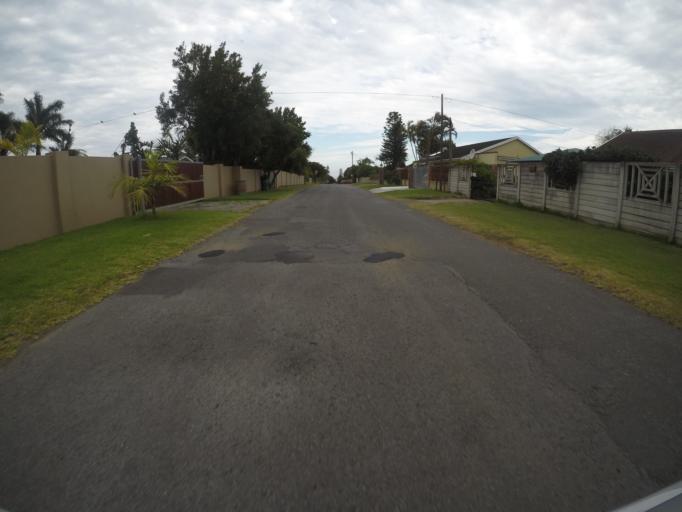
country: ZA
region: Eastern Cape
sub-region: Buffalo City Metropolitan Municipality
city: East London
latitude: -32.9429
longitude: 28.0057
